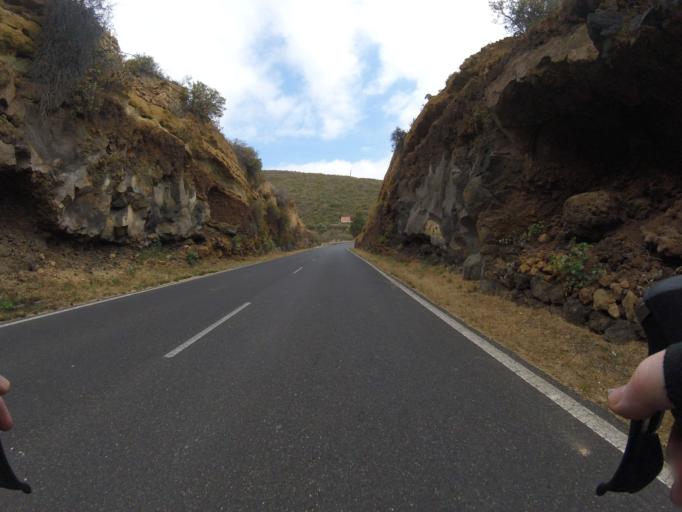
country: ES
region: Canary Islands
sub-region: Provincia de Santa Cruz de Tenerife
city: Guimar
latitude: 28.2885
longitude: -16.4056
